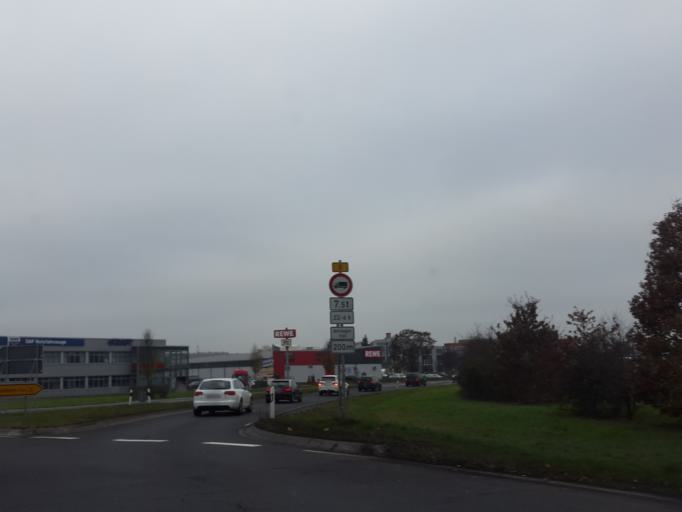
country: DE
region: Bavaria
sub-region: Regierungsbezirk Unterfranken
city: Kleinostheim
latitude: 49.9933
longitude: 9.0723
